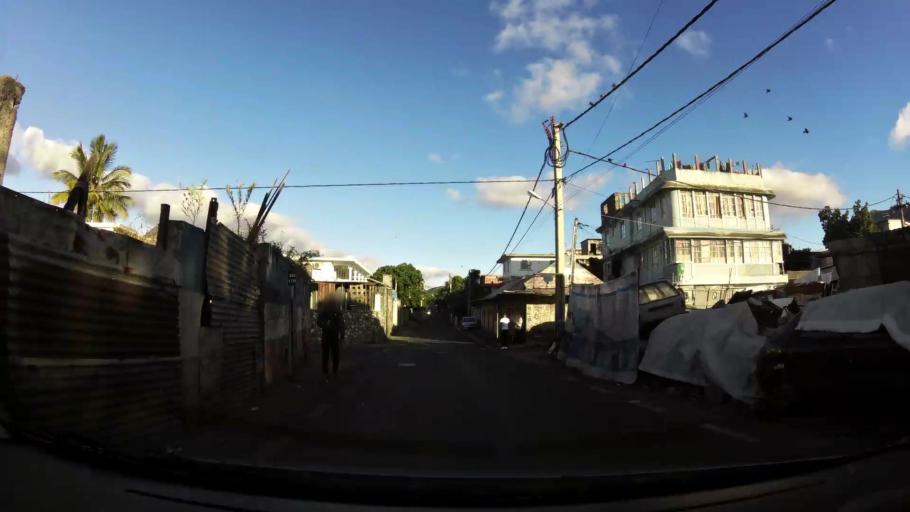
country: MU
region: Plaines Wilhems
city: Quatre Bornes
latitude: -20.2478
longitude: 57.4688
